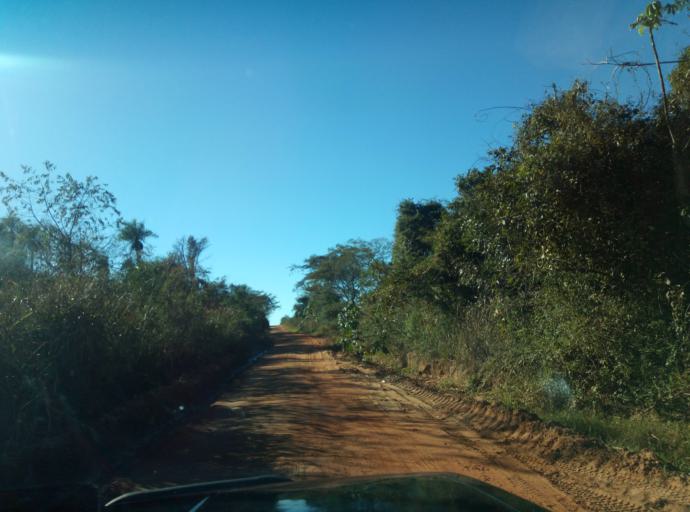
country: PY
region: Caaguazu
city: Doctor Cecilio Baez
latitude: -25.1589
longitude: -56.2897
